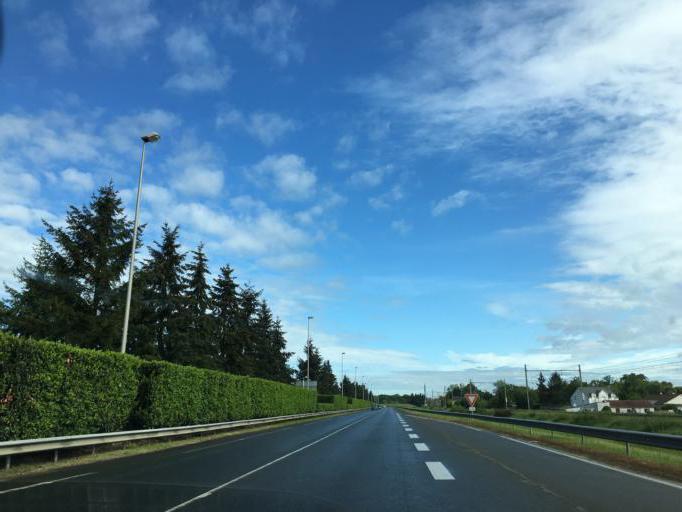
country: FR
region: Centre
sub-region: Departement du Loiret
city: Saint-Jean-le-Blanc
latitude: 47.8743
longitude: 1.9301
